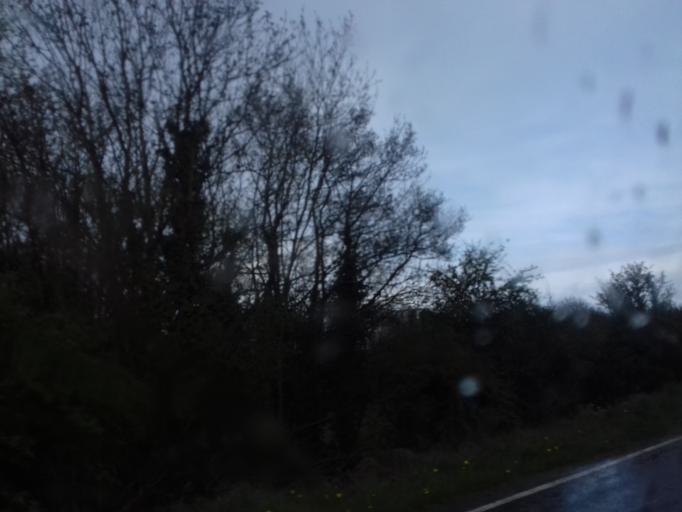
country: IE
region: Ulster
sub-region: County Donegal
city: Donegal
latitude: 54.4727
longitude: -7.9089
